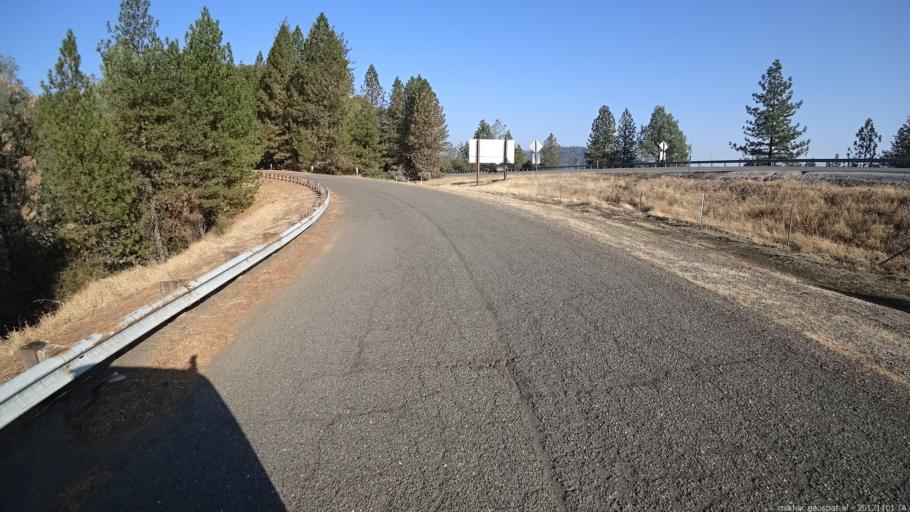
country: US
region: California
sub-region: Shasta County
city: Shasta Lake
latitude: 40.7914
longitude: -122.3240
